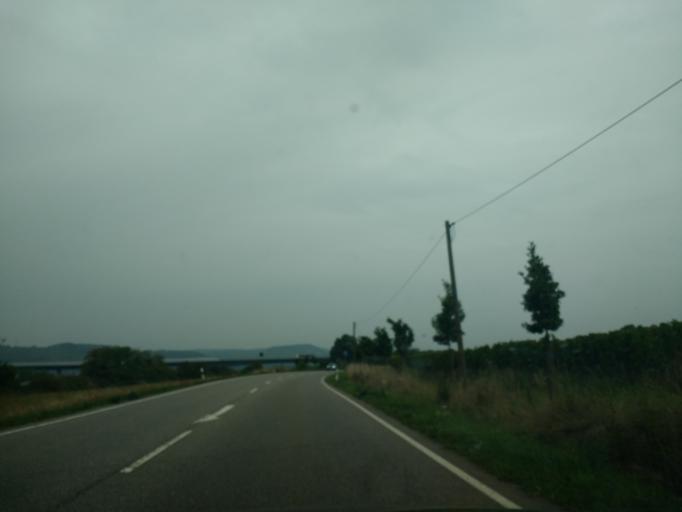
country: LU
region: Grevenmacher
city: Schengen
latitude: 49.4747
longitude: 6.3710
